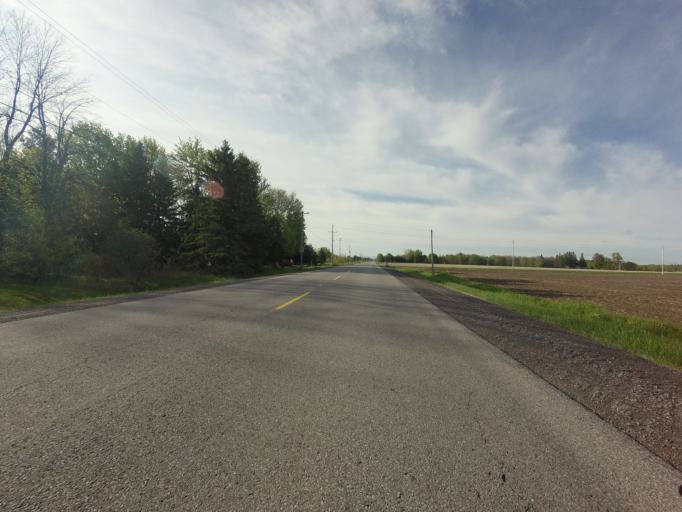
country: CA
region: Ontario
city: Ottawa
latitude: 45.2896
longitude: -75.4479
